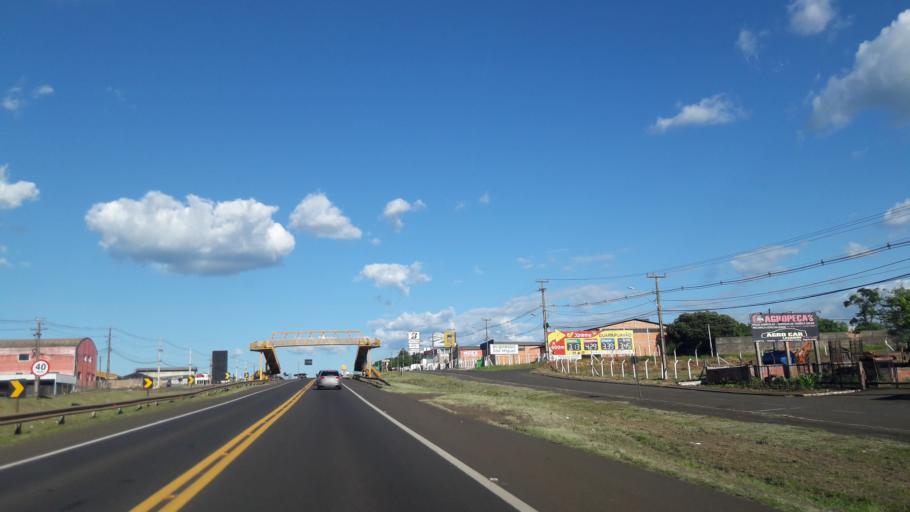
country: BR
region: Parana
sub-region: Guarapuava
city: Guarapuava
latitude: -25.3659
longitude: -51.4893
